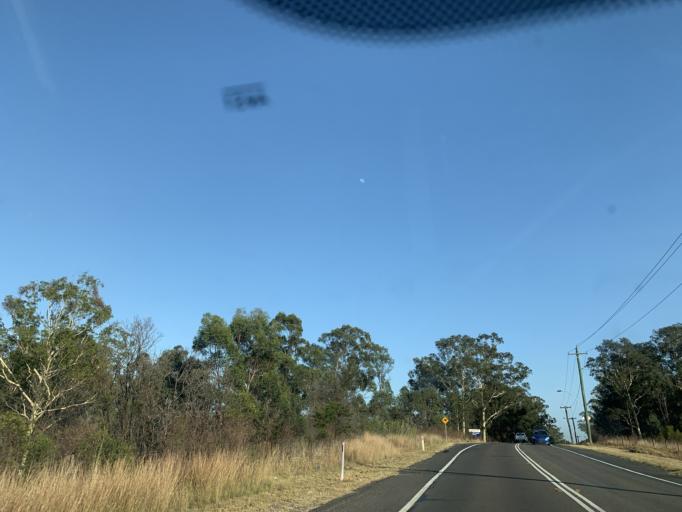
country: AU
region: New South Wales
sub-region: Fairfield
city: Horsley Park
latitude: -33.8305
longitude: 150.8733
